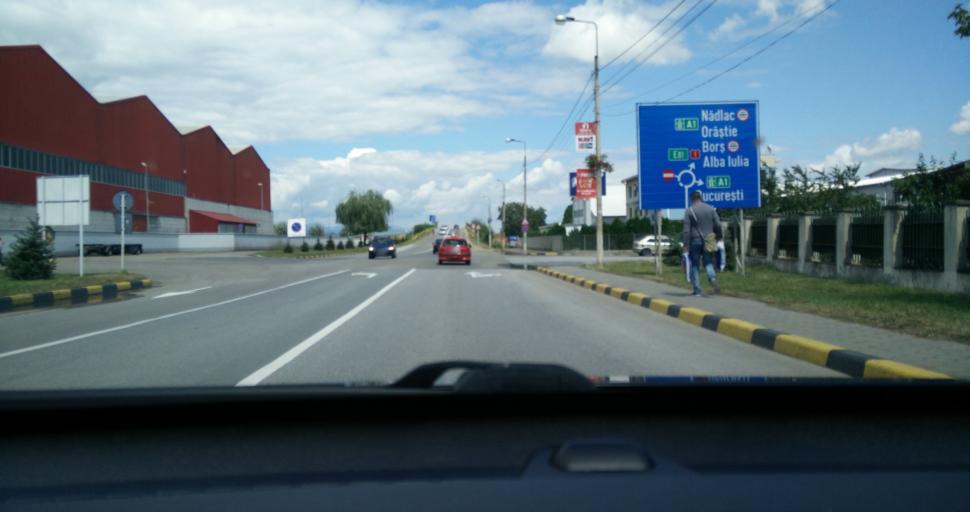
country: RO
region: Alba
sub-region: Municipiul Sebes
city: Lancram
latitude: 45.9694
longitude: 23.5576
